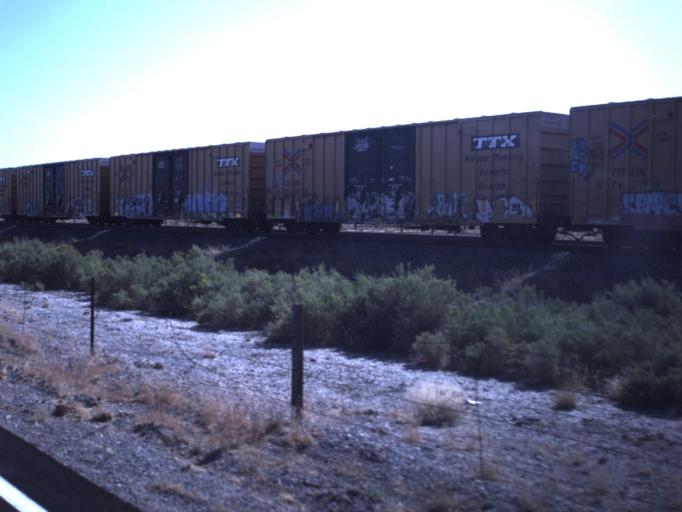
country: US
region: Utah
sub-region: Millard County
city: Delta
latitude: 39.2287
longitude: -112.6702
